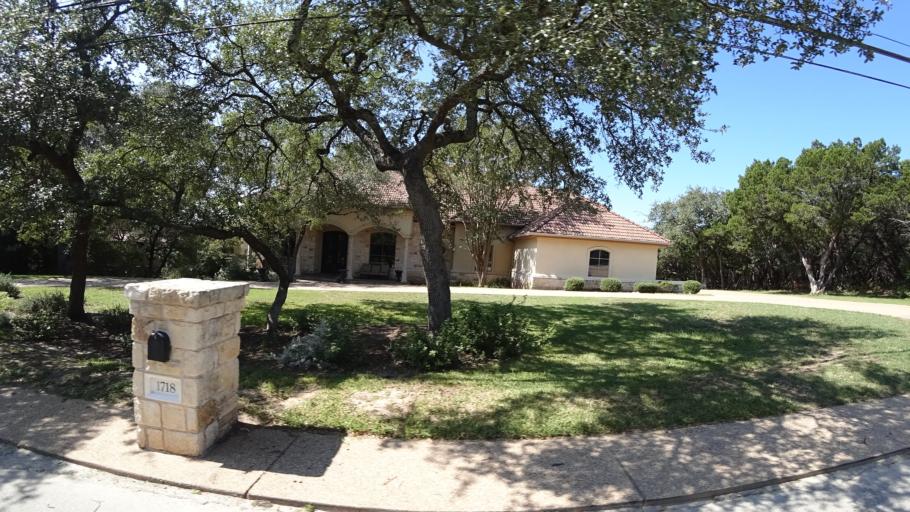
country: US
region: Texas
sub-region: Travis County
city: West Lake Hills
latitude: 30.3076
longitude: -97.7934
